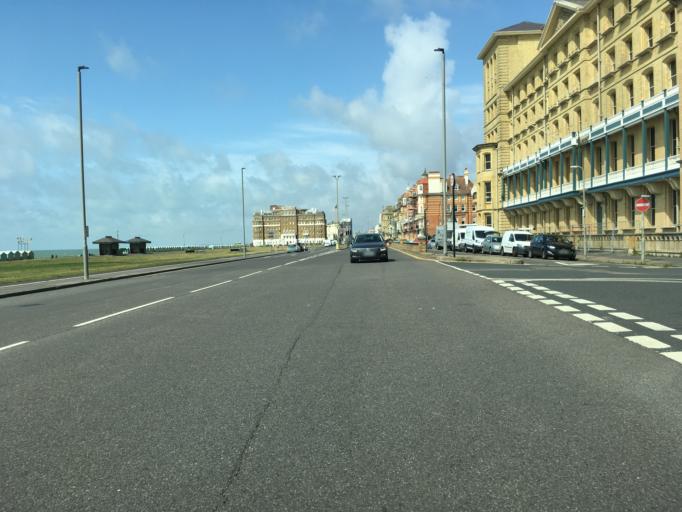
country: GB
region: England
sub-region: Brighton and Hove
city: Hove
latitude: 50.8243
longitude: -0.1675
